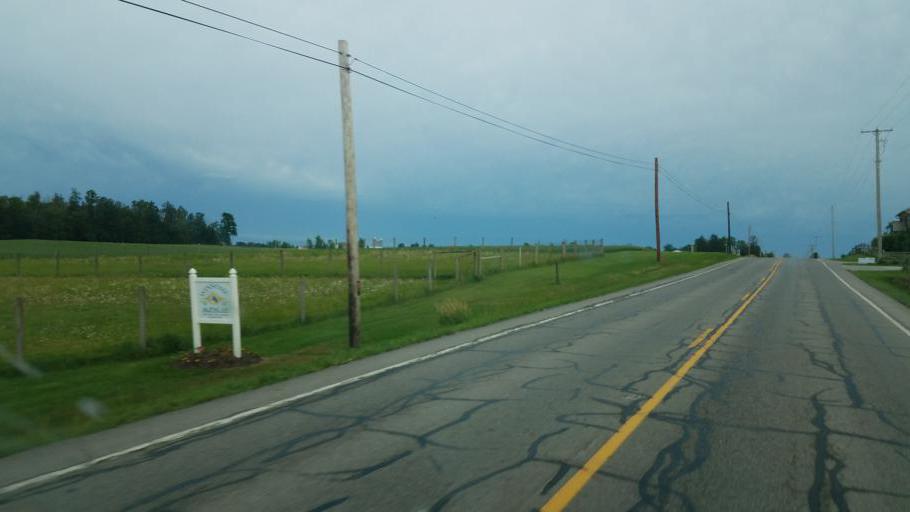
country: US
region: Ohio
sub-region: Huron County
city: Greenwich
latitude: 40.9350
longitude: -82.4955
